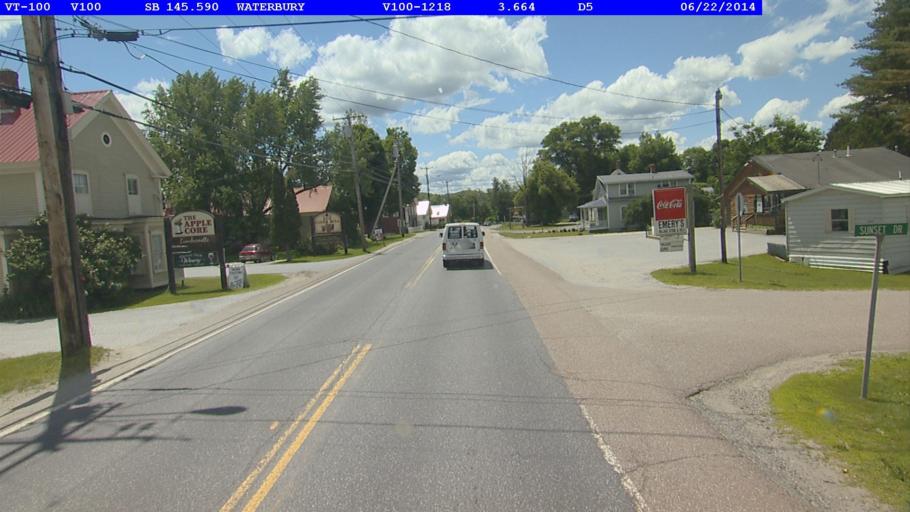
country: US
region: Vermont
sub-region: Washington County
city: Waterbury
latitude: 44.3818
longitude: -72.7206
